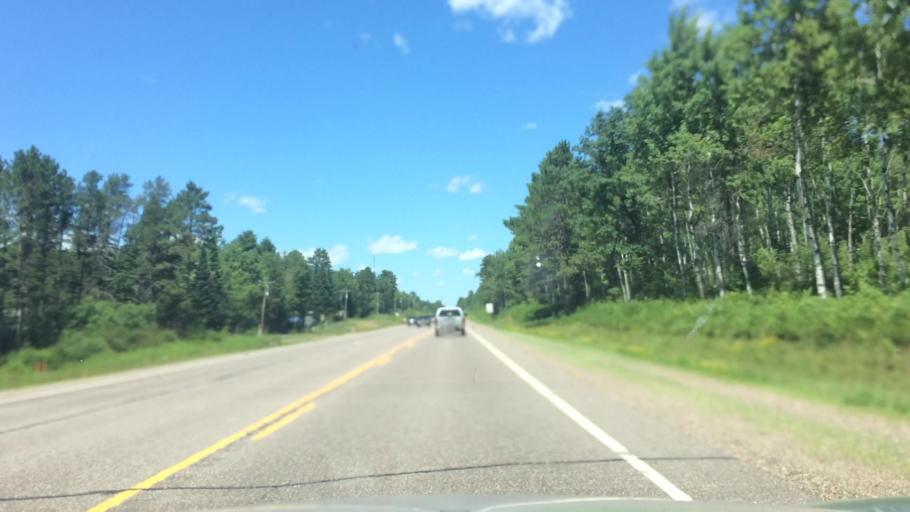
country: US
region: Wisconsin
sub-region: Lincoln County
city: Tomahawk
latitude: 45.6727
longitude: -89.7141
